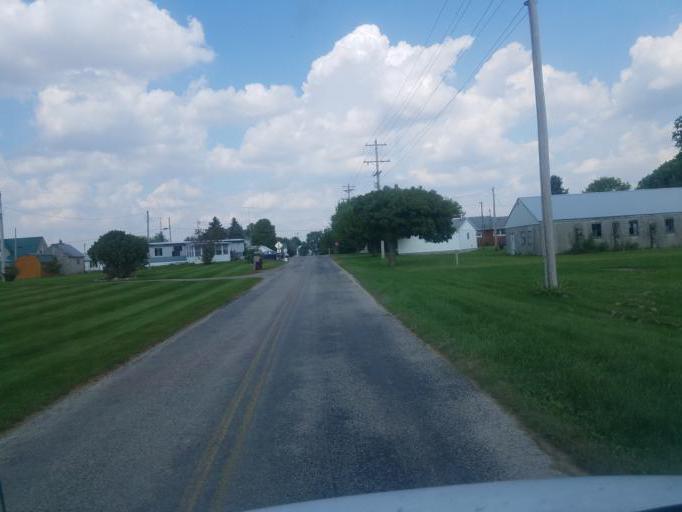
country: US
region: Ohio
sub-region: Hardin County
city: Ada
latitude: 40.6530
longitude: -83.8931
